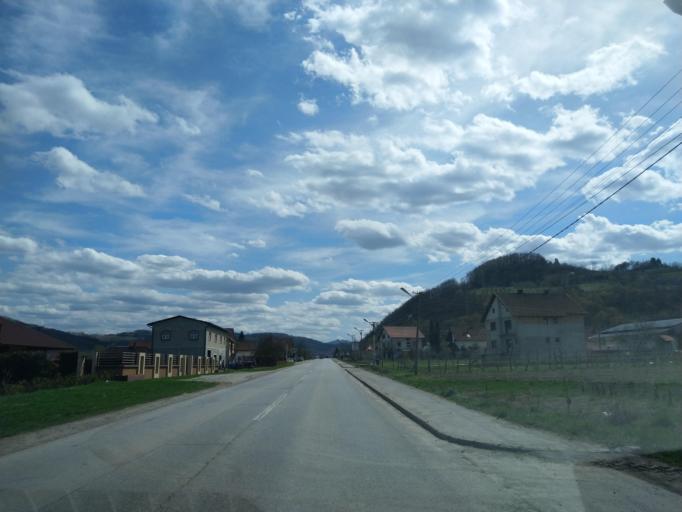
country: RS
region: Central Serbia
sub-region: Zlatiborski Okrug
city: Arilje
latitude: 43.7020
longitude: 20.1196
